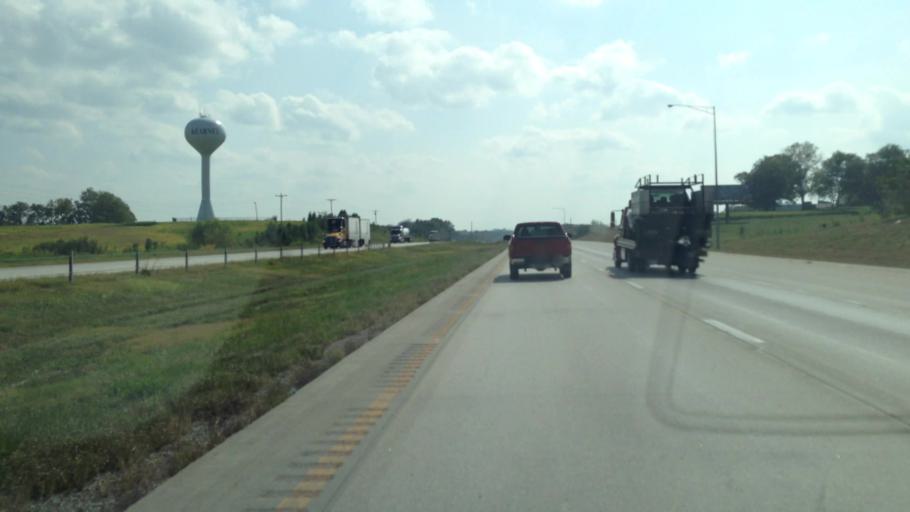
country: US
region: Missouri
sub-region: Clay County
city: Kearney
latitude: 39.3630
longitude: -94.3751
